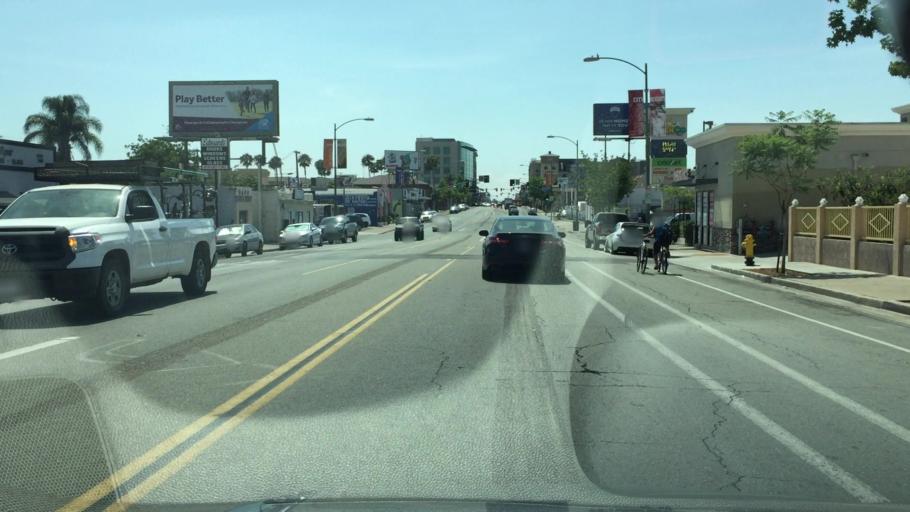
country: US
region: California
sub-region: San Diego County
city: Lemon Grove
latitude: 32.7496
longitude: -117.0968
